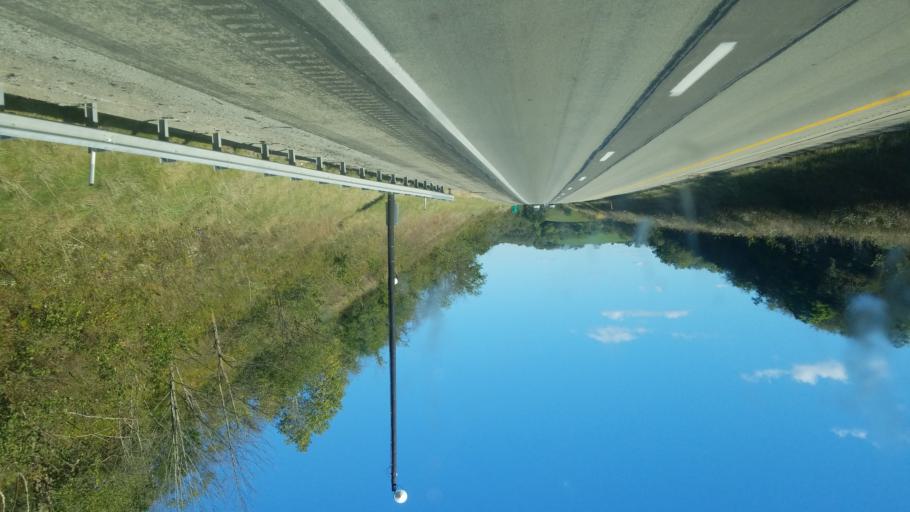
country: US
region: Pennsylvania
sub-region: Washington County
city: East Washington
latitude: 40.0750
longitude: -80.1906
